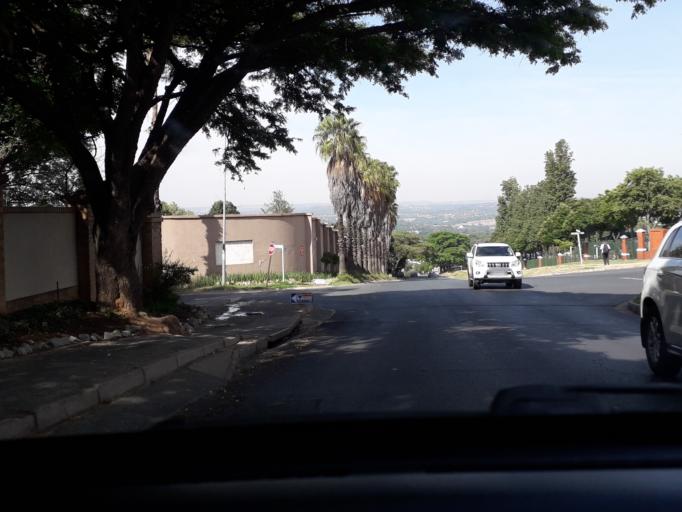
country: ZA
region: Gauteng
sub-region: City of Johannesburg Metropolitan Municipality
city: Diepsloot
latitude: -26.0442
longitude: 28.0133
